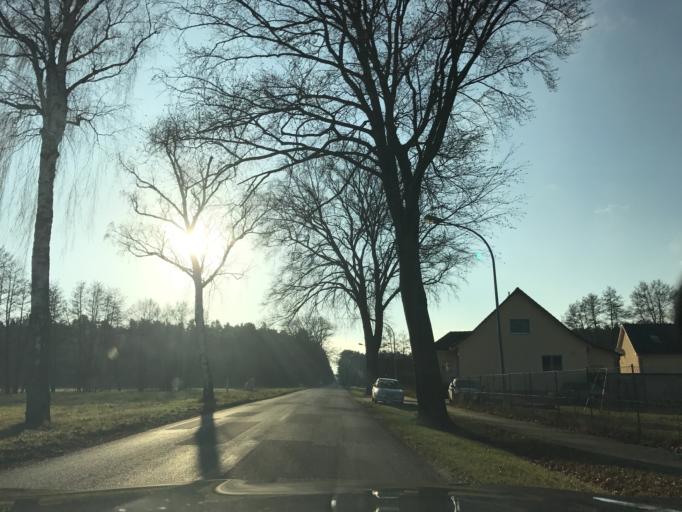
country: DE
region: Brandenburg
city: Wenzlow
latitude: 52.2947
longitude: 12.4537
